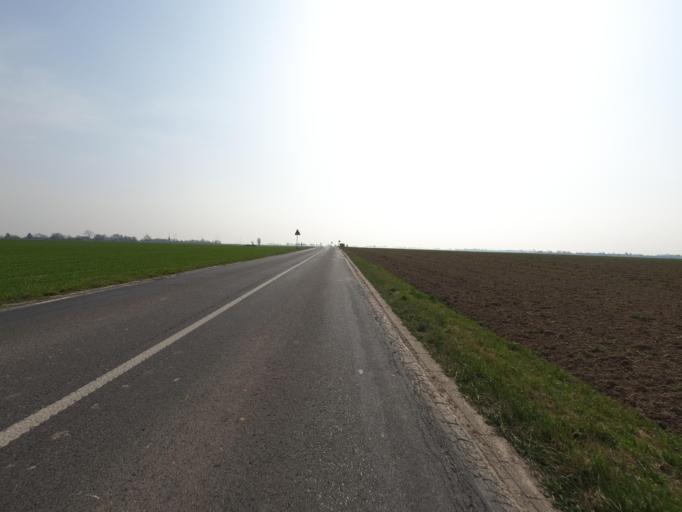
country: DE
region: North Rhine-Westphalia
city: Erkelenz
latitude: 51.0095
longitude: 6.3396
